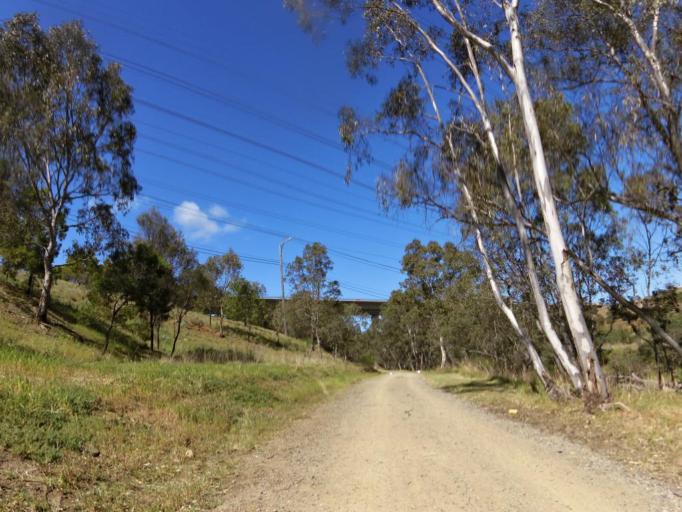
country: AU
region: Victoria
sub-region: Brimbank
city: Kealba
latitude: -37.7436
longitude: 144.8389
